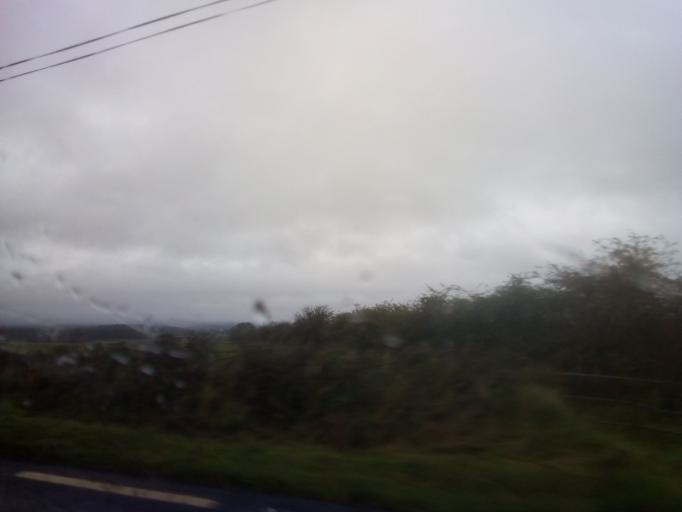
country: IE
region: Connaught
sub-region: Roscommon
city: Boyle
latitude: 53.8215
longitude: -8.3518
